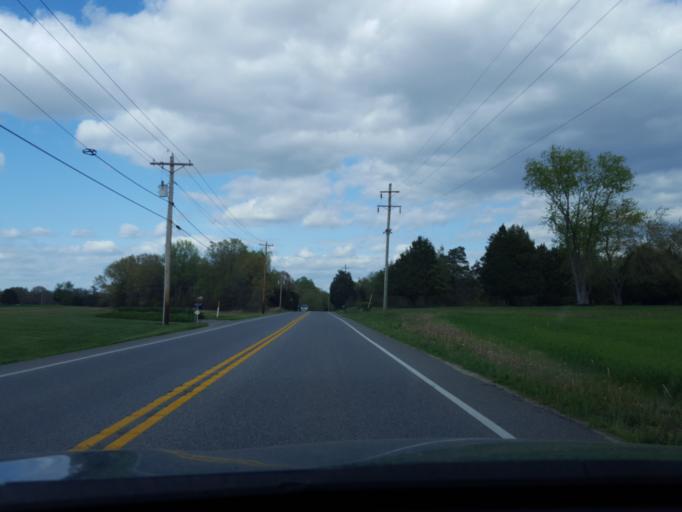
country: US
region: Maryland
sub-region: Charles County
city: Saint Charles
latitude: 38.5625
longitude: -76.8651
